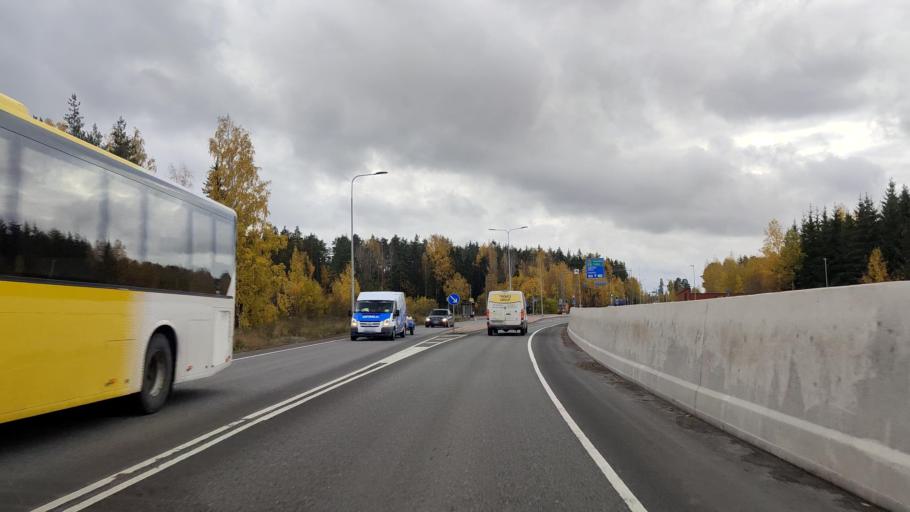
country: FI
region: Varsinais-Suomi
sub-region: Turku
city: Kaarina
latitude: 60.4298
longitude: 22.3844
